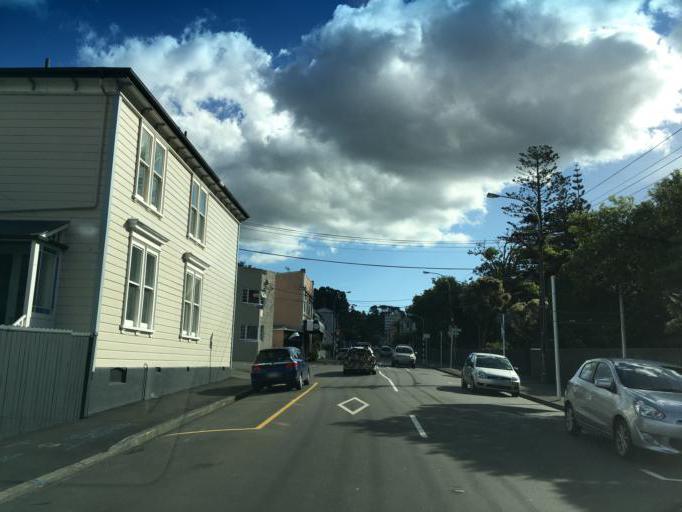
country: NZ
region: Wellington
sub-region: Wellington City
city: Kelburn
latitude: -41.2765
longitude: 174.7720
